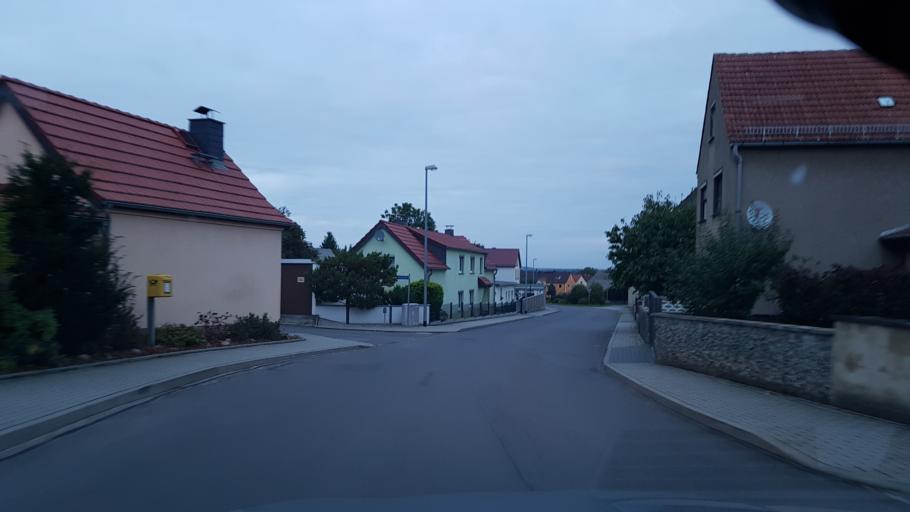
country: DE
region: Brandenburg
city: Hirschfeld
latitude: 51.3832
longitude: 13.6143
